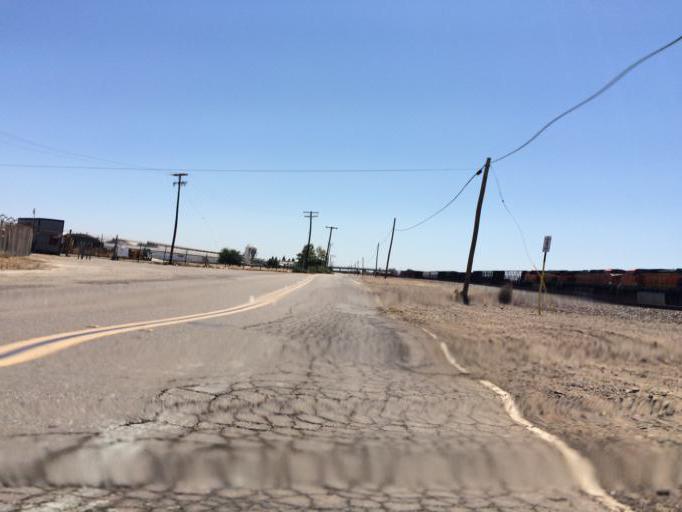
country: US
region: California
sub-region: Fresno County
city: Fresno
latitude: 36.7129
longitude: -119.7713
